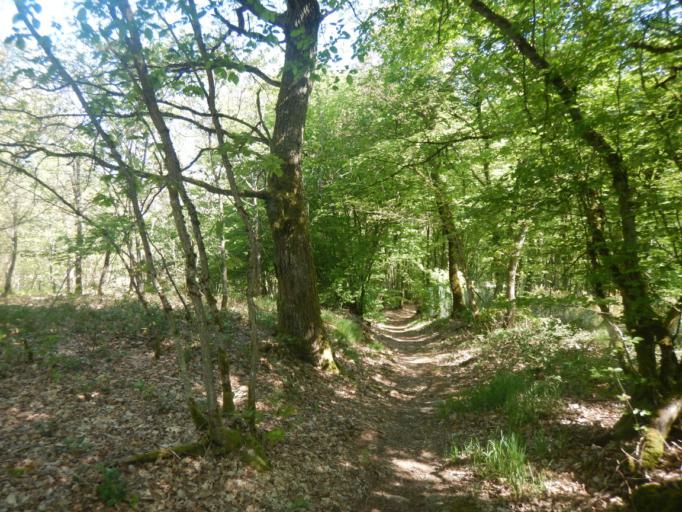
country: LU
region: Diekirch
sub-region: Canton de Diekirch
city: Bourscheid
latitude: 49.9107
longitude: 6.0849
